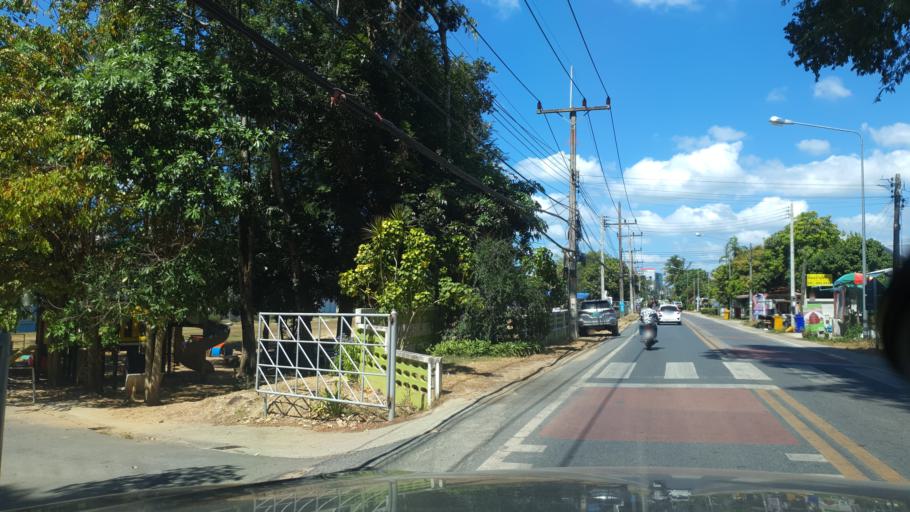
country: TH
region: Phuket
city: Thalang
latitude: 8.1313
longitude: 98.3076
